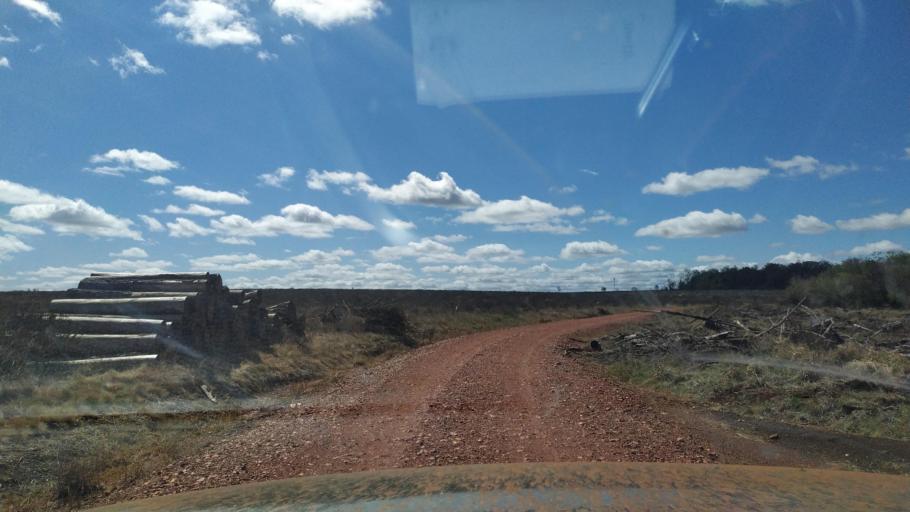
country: AR
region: Corrientes
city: Gobernador Ingeniero Valentin Virasoro
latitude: -28.2918
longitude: -56.0520
